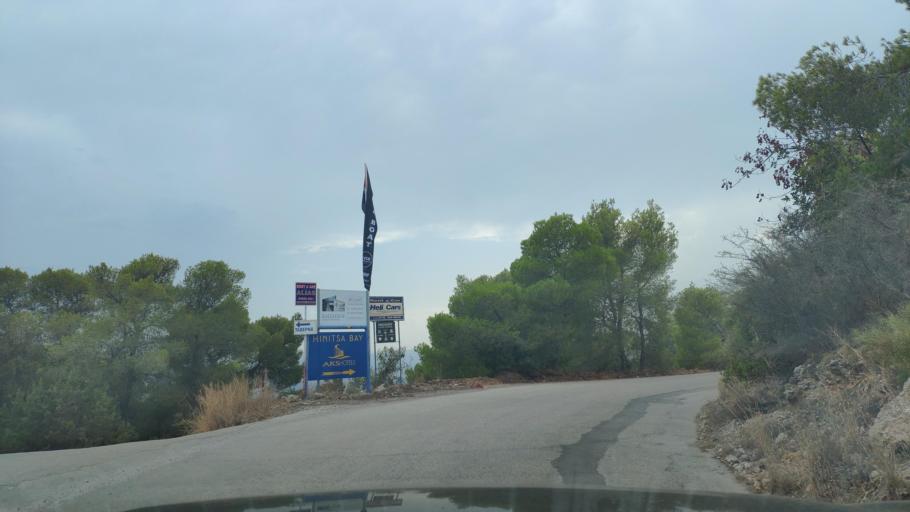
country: GR
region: Peloponnese
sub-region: Nomos Argolidos
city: Porto Cheli
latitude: 37.3070
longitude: 23.1520
